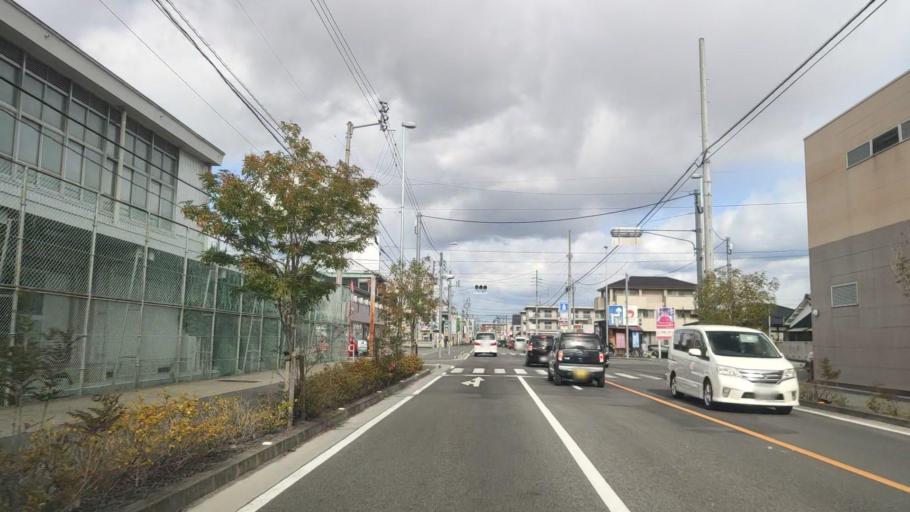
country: JP
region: Ehime
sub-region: Shikoku-chuo Shi
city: Matsuyama
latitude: 33.8113
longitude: 132.7608
